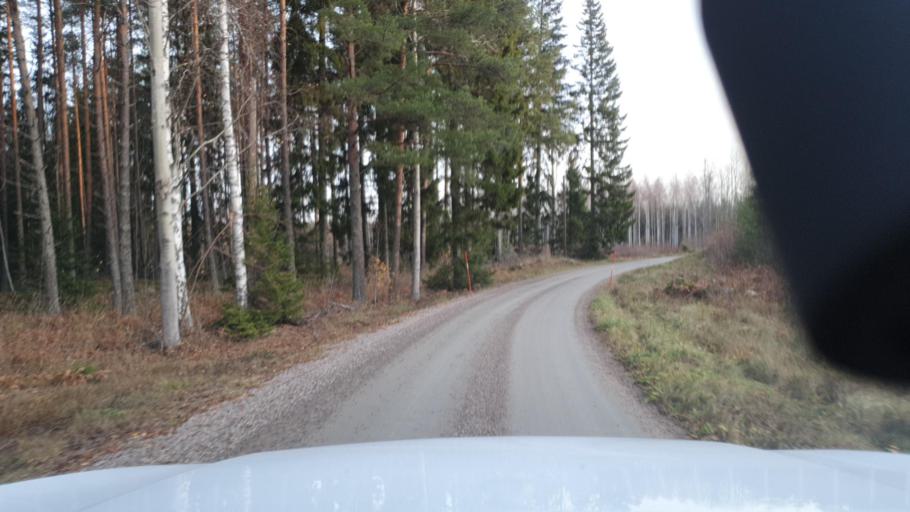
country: SE
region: Uppsala
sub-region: Alvkarleby Kommun
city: AElvkarleby
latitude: 60.4835
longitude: 17.5047
